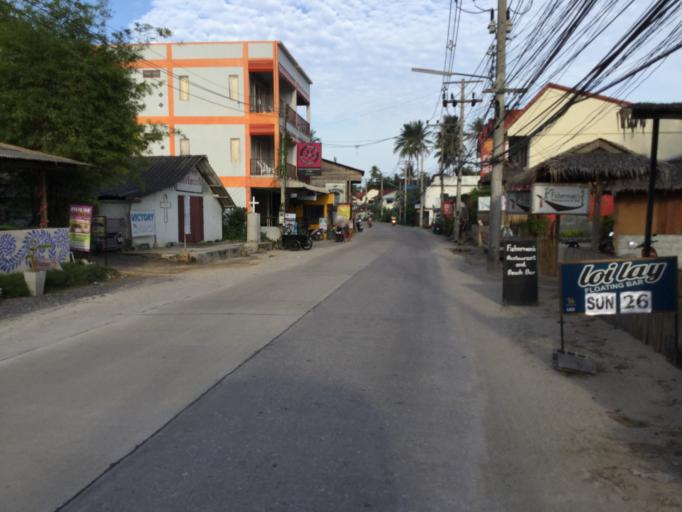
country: TH
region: Surat Thani
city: Ko Pha-Ngan
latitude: 9.7005
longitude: 100.0202
